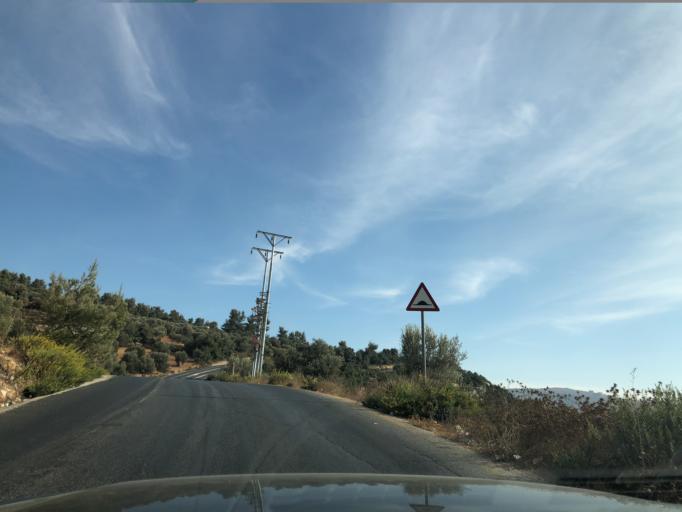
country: JO
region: Irbid
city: `Ayn Jannah
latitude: 32.3251
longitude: 35.7604
